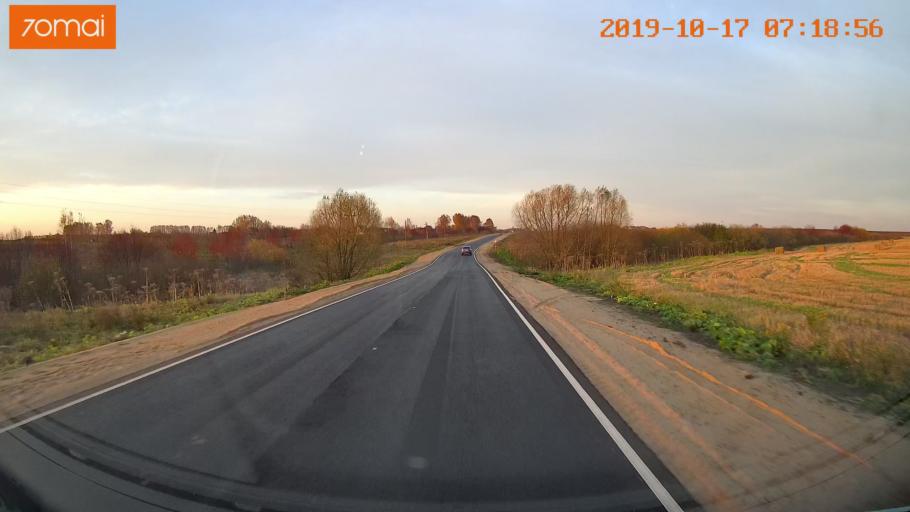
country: RU
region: Ivanovo
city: Gavrilov Posad
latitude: 56.3489
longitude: 40.2094
